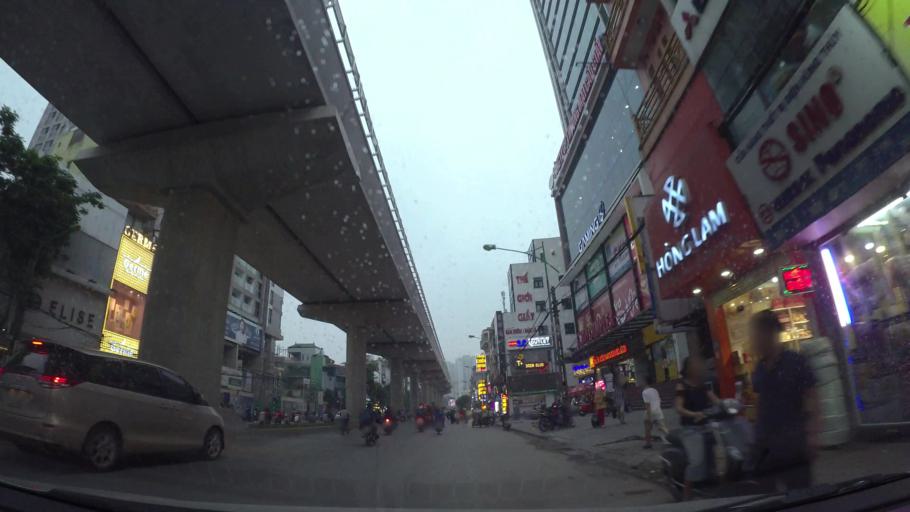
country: VN
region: Ha Noi
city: Cau Giay
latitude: 21.0323
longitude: 105.7990
